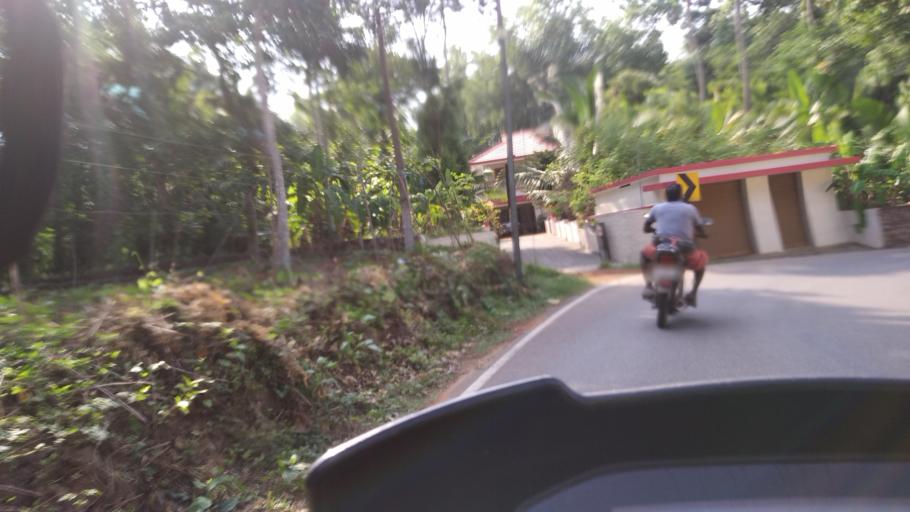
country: IN
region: Kerala
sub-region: Ernakulam
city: Piravam
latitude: 9.8590
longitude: 76.5198
